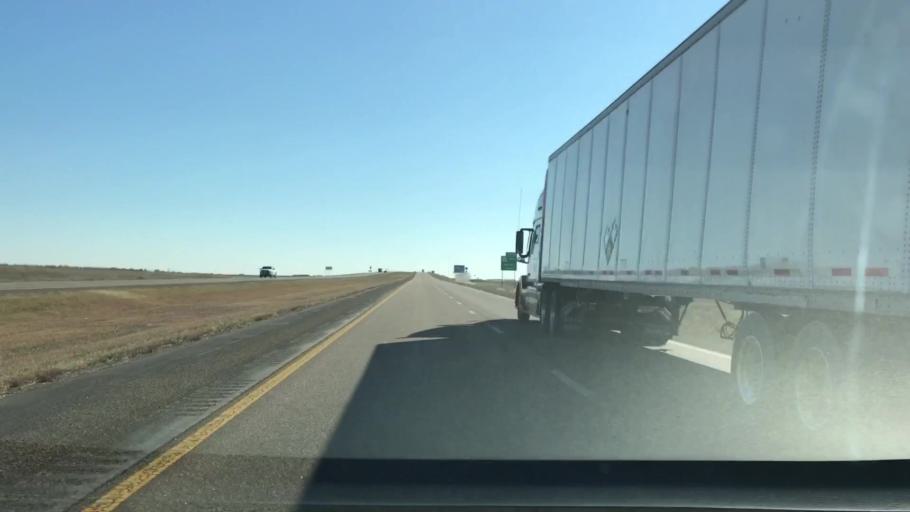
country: US
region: Kansas
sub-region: Logan County
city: Oakley
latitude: 39.1310
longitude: -100.8186
